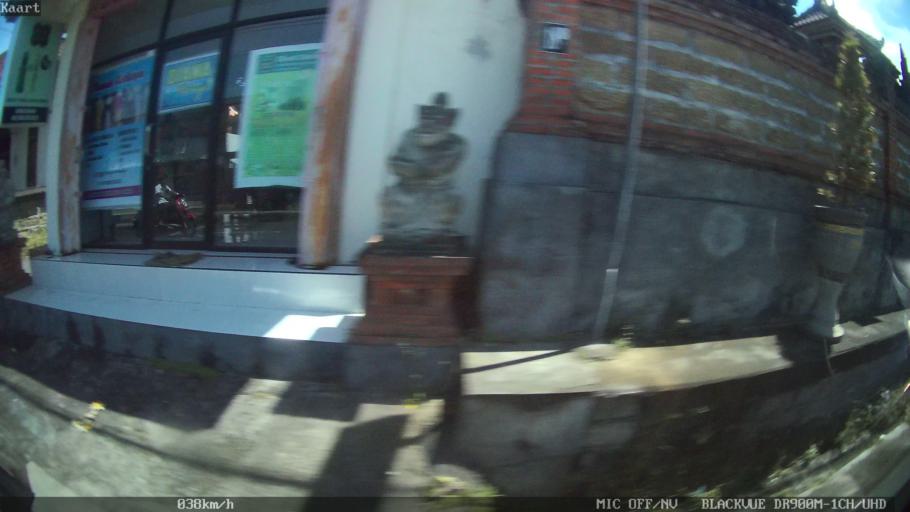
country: ID
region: Bali
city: Banjar Kelodan
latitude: -8.5474
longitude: 115.3347
